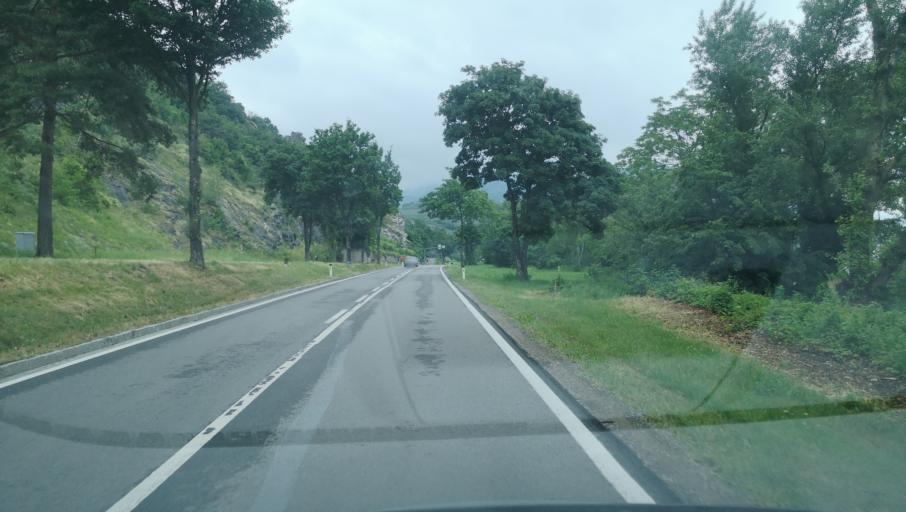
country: AT
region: Lower Austria
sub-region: Politischer Bezirk Krems
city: Spitz
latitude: 48.3518
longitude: 15.4061
